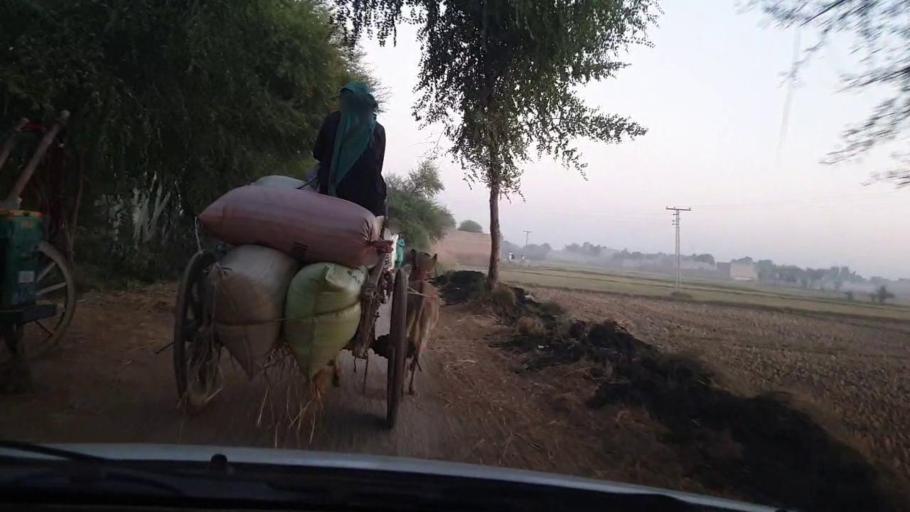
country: PK
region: Sindh
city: Khairpur Nathan Shah
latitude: 27.1466
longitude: 67.7024
